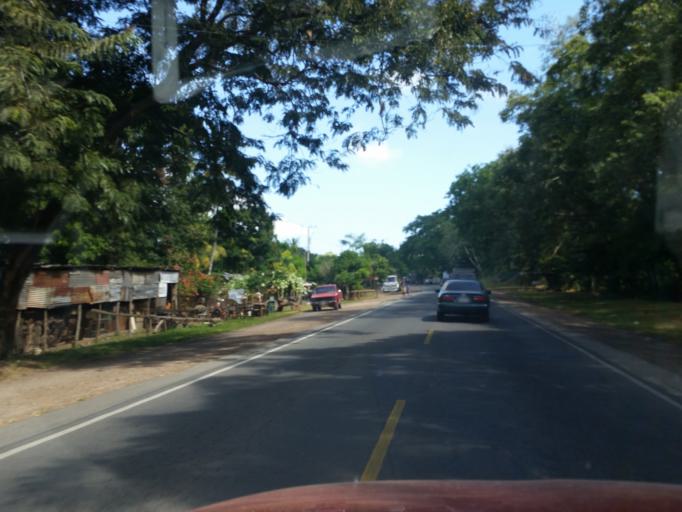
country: NI
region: Granada
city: Diriomo
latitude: 11.8478
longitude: -86.0244
